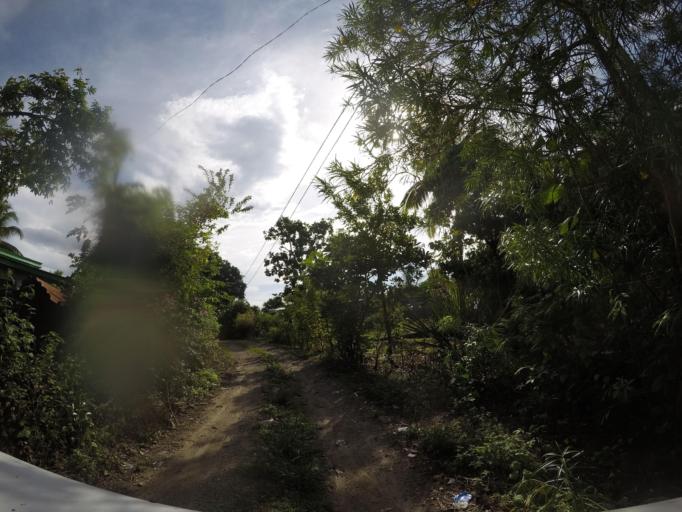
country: TL
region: Baucau
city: Baucau
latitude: -8.5060
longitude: 126.4477
